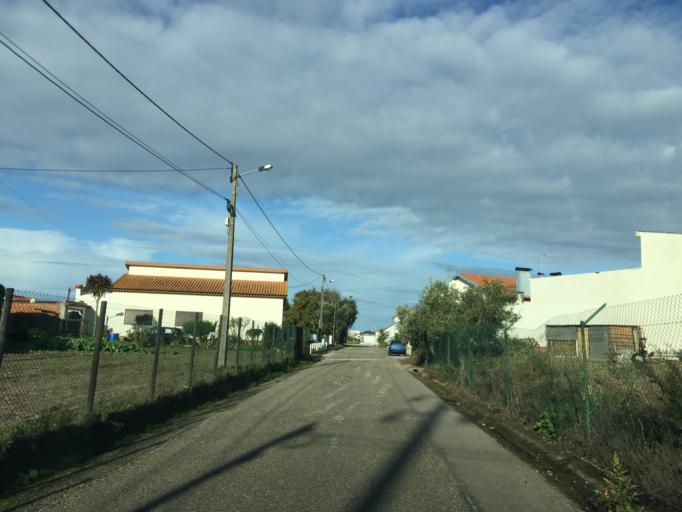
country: PT
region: Coimbra
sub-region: Figueira da Foz
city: Lavos
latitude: 40.0630
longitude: -8.8157
